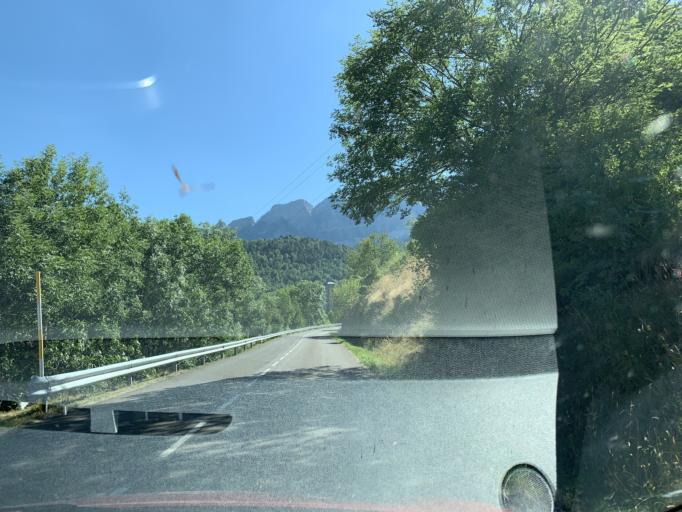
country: ES
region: Aragon
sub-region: Provincia de Huesca
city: Hoz de Jaca
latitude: 42.6984
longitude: -0.3228
